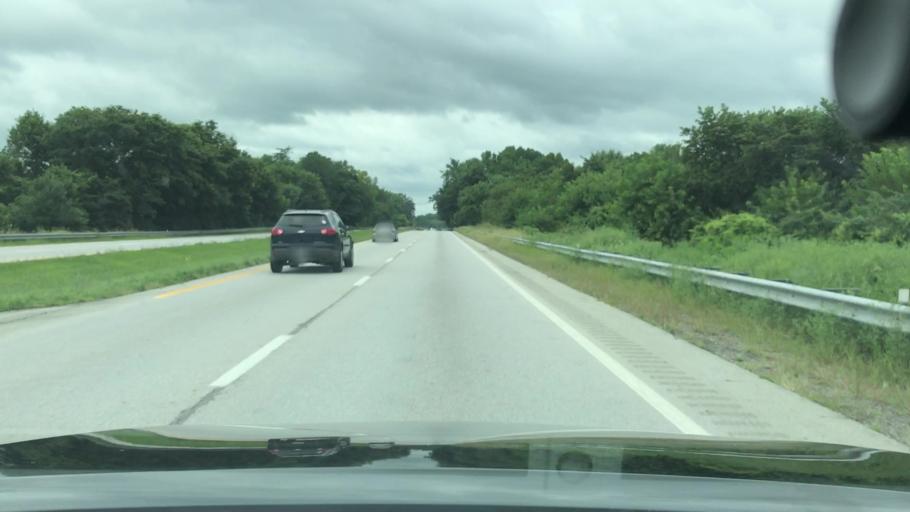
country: US
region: Ohio
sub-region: Pickaway County
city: Commercial Point
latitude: 39.8097
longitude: -82.9958
